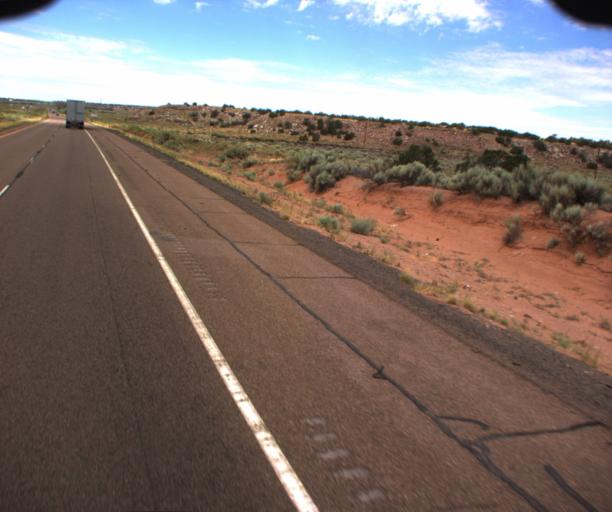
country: US
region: Arizona
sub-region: Apache County
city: Houck
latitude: 35.1805
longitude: -109.4617
